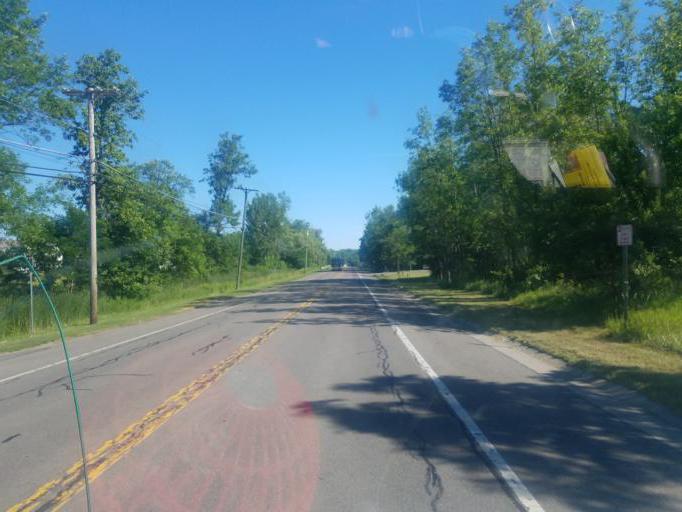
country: US
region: New York
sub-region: Ontario County
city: Canandaigua
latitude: 42.8685
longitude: -77.2506
